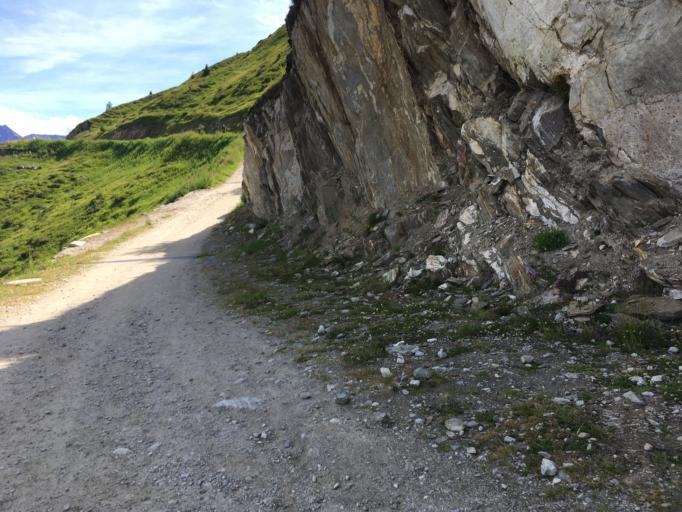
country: CH
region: Valais
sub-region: Goms District
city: Fiesch
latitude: 46.4207
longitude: 8.1106
